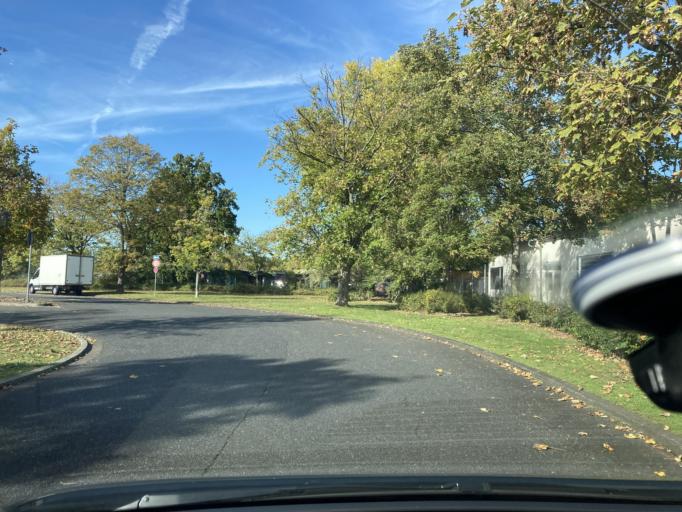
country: DE
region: Hesse
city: Niederrad
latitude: 50.1081
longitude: 8.6159
